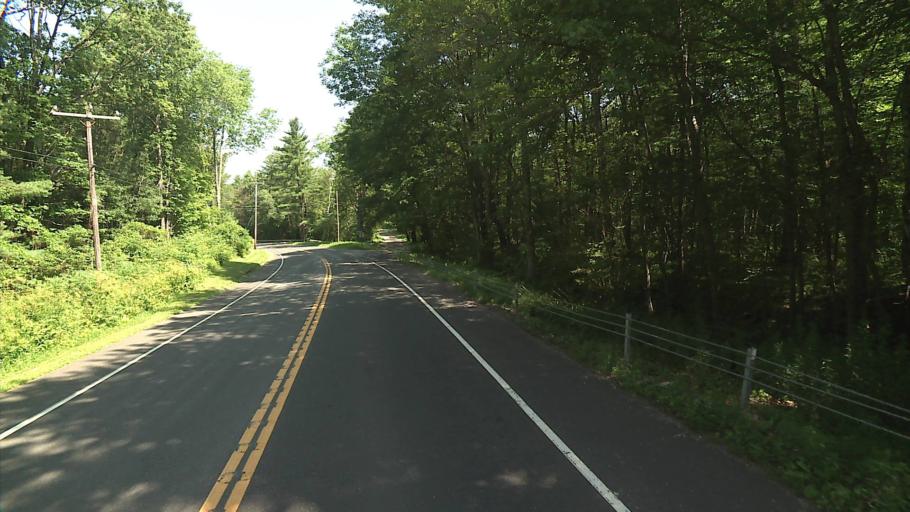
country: US
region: Massachusetts
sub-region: Berkshire County
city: New Marlborough
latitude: 42.0327
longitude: -73.2069
